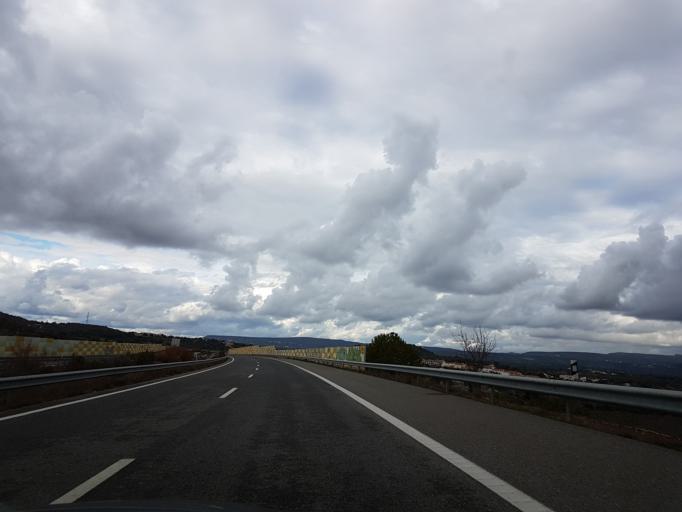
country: PT
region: Faro
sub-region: Albufeira
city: Ferreiras
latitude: 37.1682
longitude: -8.2149
